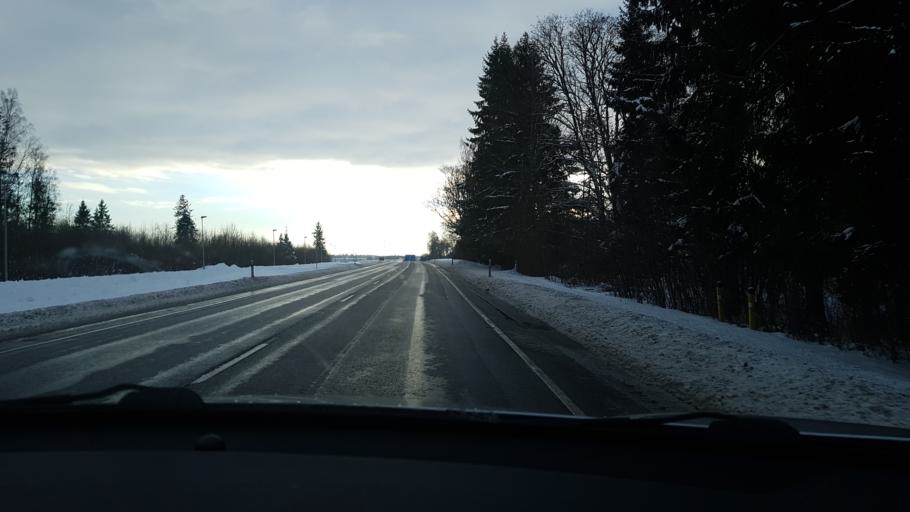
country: EE
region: Jaervamaa
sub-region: Paide linn
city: Paide
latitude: 58.9268
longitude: 25.6280
